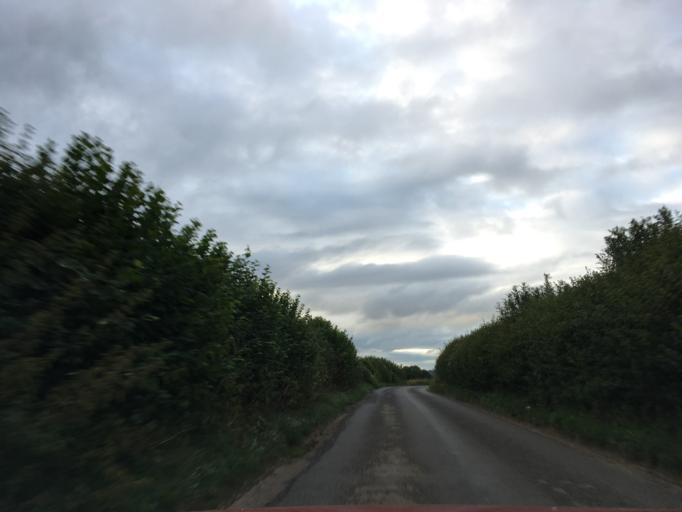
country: GB
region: England
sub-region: Wiltshire
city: Biddestone
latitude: 51.4660
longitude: -2.2023
